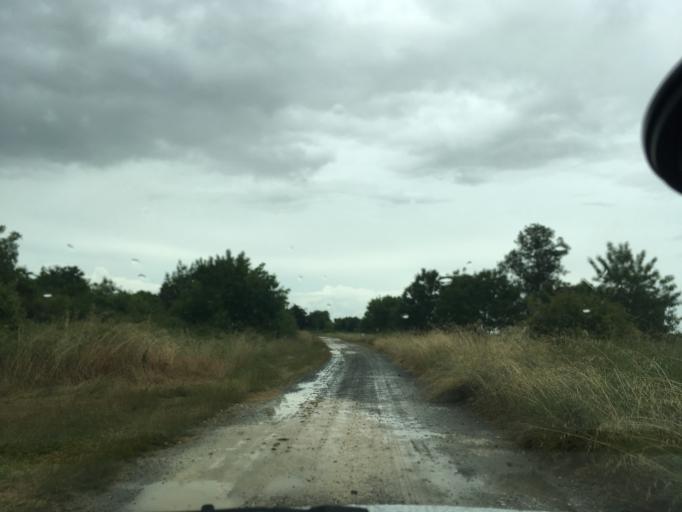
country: FR
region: Aquitaine
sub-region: Departement de la Gironde
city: Saint-Estephe
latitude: 45.3364
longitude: -0.7990
